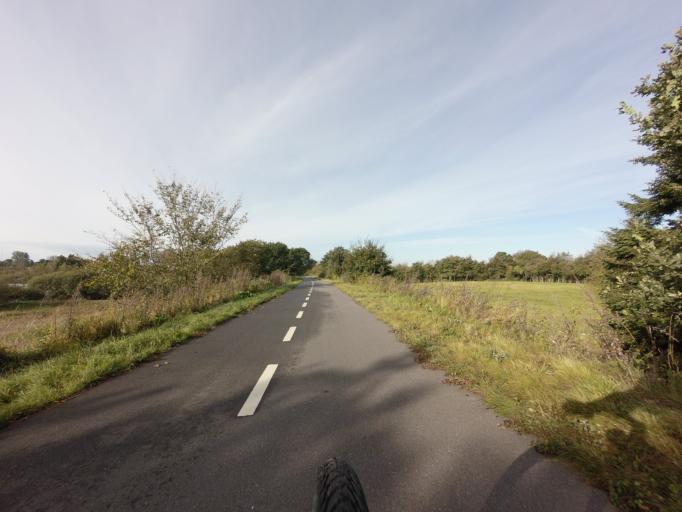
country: DK
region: Central Jutland
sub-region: Viborg Kommune
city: Viborg
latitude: 56.4284
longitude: 9.4130
